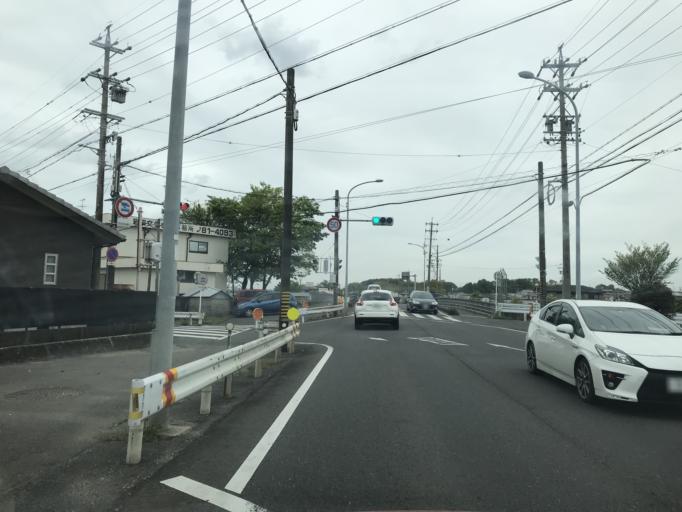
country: JP
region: Aichi
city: Kasugai
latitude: 35.2751
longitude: 136.9839
